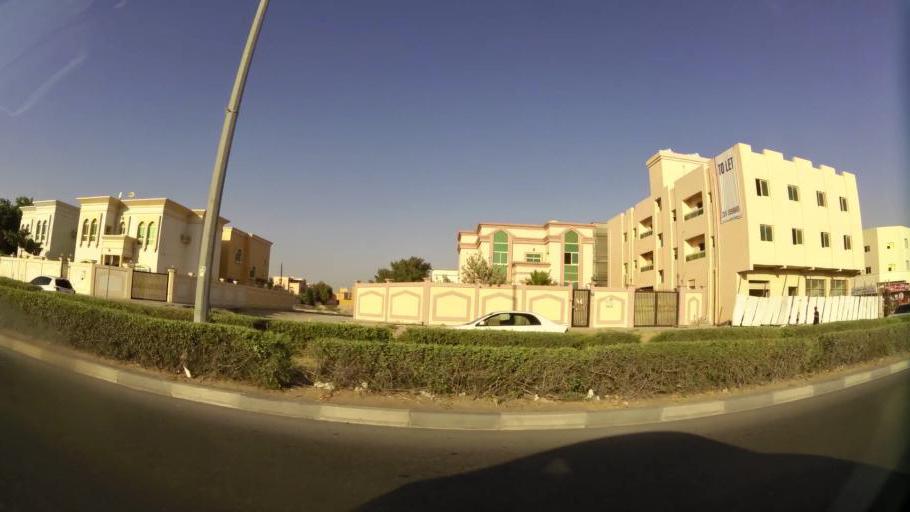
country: AE
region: Ajman
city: Ajman
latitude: 25.3913
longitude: 55.5059
